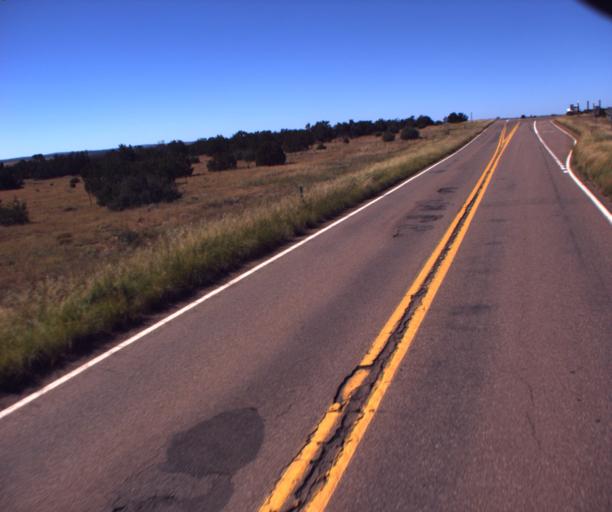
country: US
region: Arizona
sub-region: Navajo County
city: Heber-Overgaard
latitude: 34.4814
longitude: -110.3365
